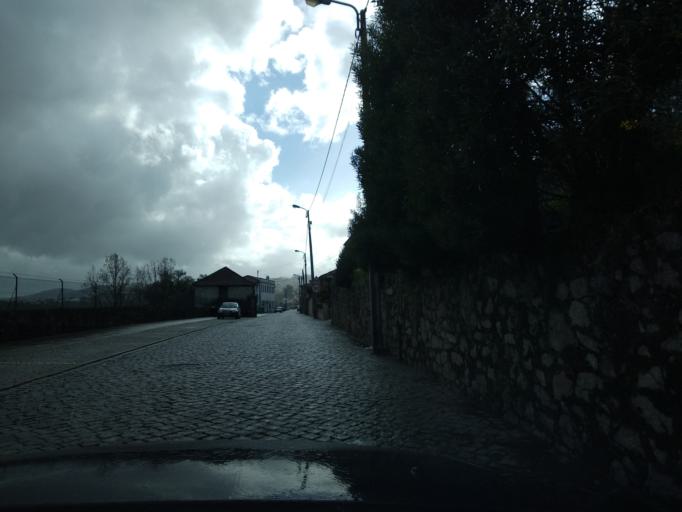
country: PT
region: Porto
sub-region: Paredes
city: Madalena
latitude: 41.2408
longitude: -8.3363
